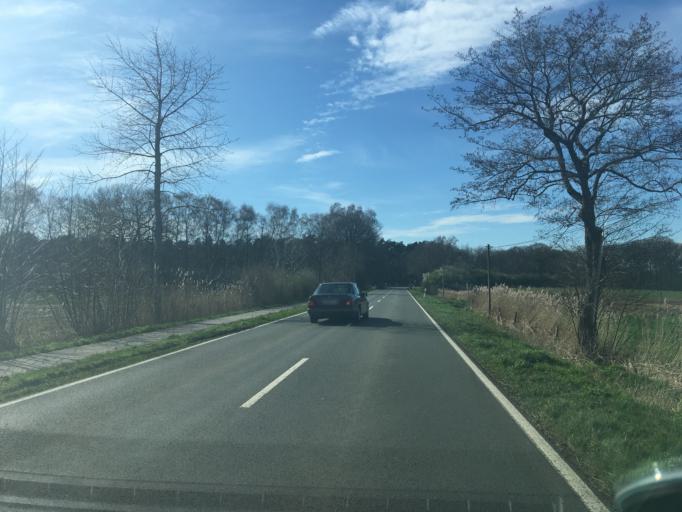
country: DE
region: North Rhine-Westphalia
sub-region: Regierungsbezirk Munster
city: Isselburg
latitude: 51.8410
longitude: 6.5080
